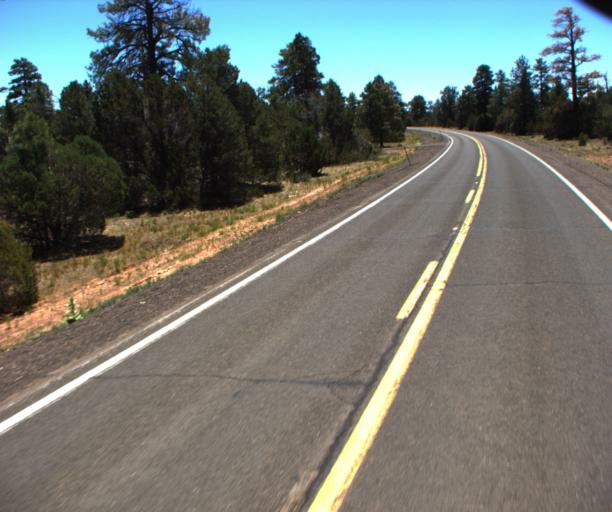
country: US
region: Arizona
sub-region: Gila County
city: Star Valley
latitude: 34.6767
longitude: -111.1120
